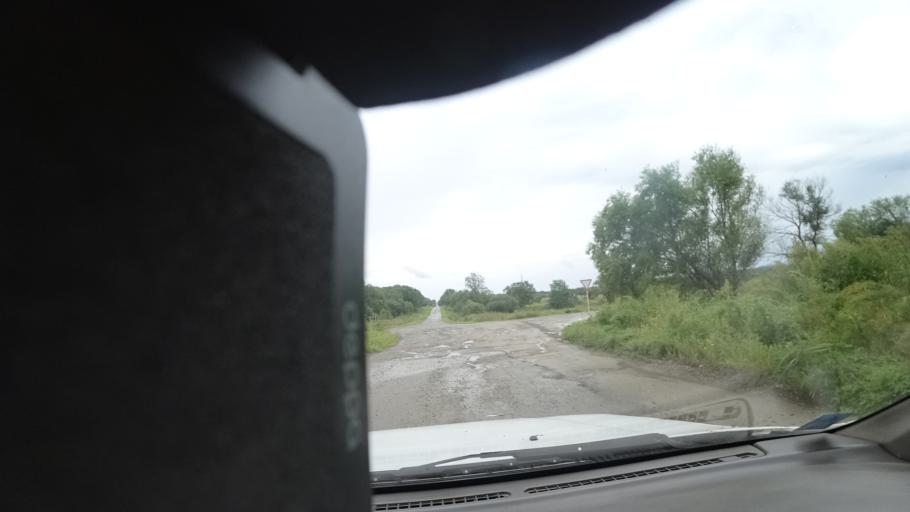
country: RU
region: Primorskiy
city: Lazo
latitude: 45.8700
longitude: 133.6904
